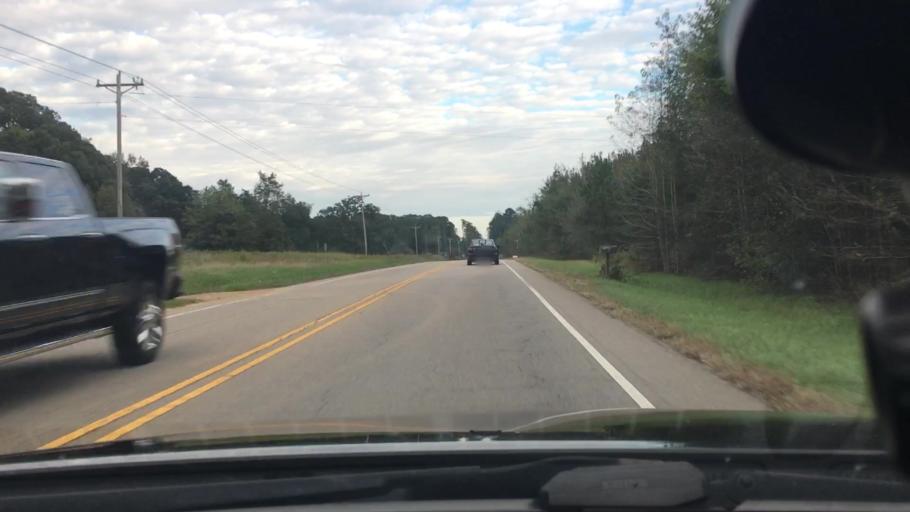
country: US
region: North Carolina
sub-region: Moore County
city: Robbins
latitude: 35.3967
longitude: -79.5339
